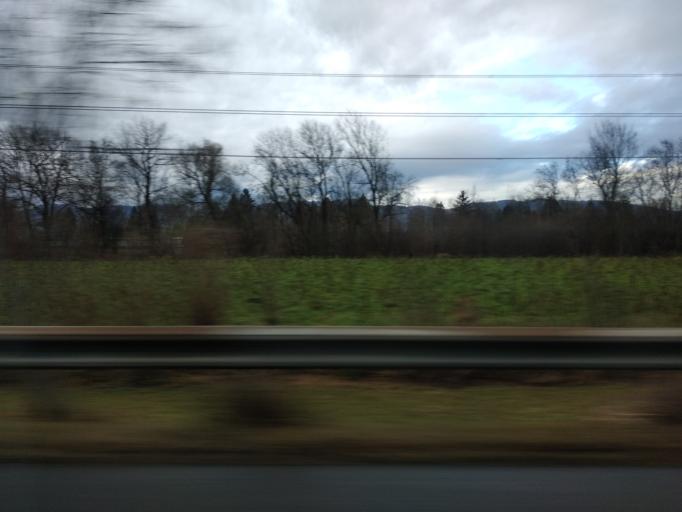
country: AT
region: Vorarlberg
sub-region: Politischer Bezirk Dornbirn
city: Hohenems
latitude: 47.3805
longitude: 9.6753
